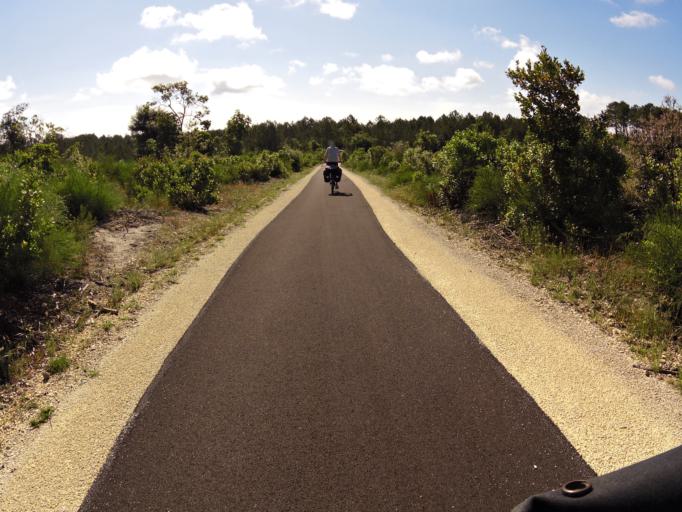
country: FR
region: Aquitaine
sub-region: Departement de la Gironde
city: Lacanau
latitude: 45.0326
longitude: -1.1787
